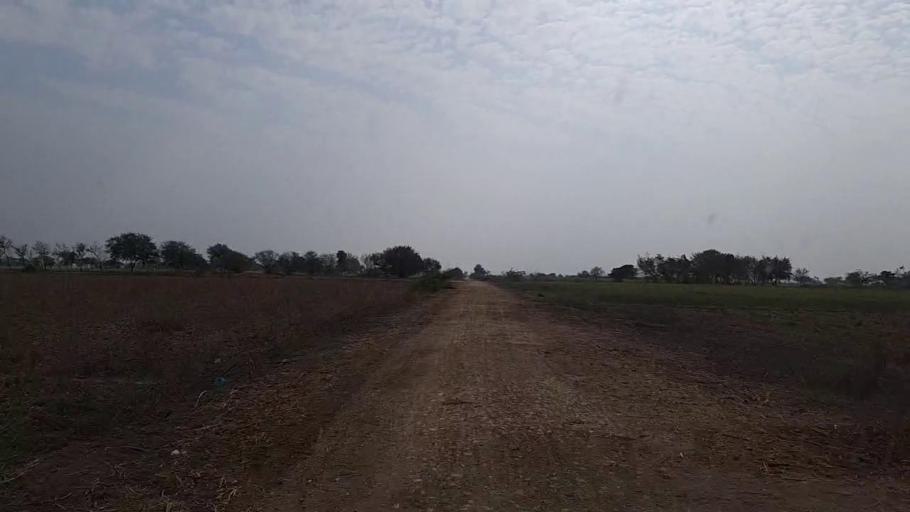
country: PK
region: Sindh
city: Mirwah Gorchani
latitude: 25.3962
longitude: 69.1018
